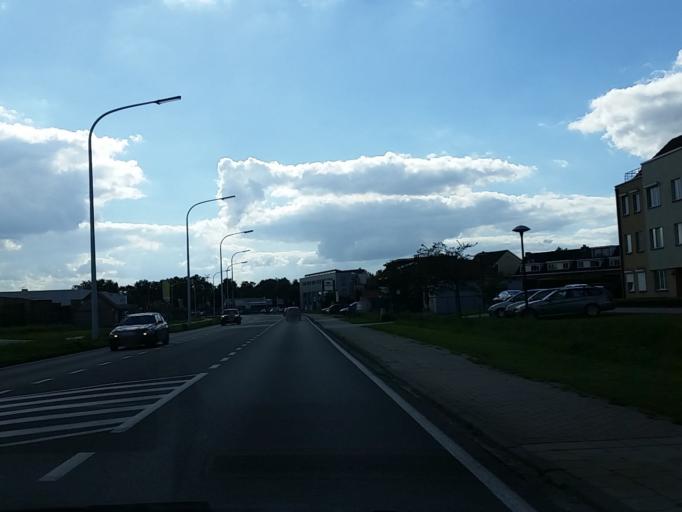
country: BE
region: Flanders
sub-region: Provincie Antwerpen
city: Kontich
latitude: 51.1256
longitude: 4.4515
